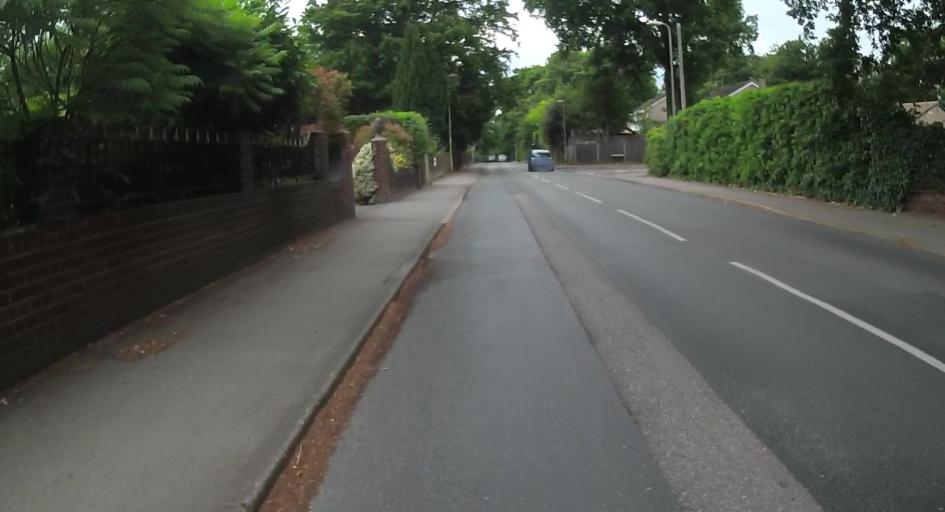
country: GB
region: England
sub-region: Hampshire
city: Fleet
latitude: 51.2596
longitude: -0.8418
